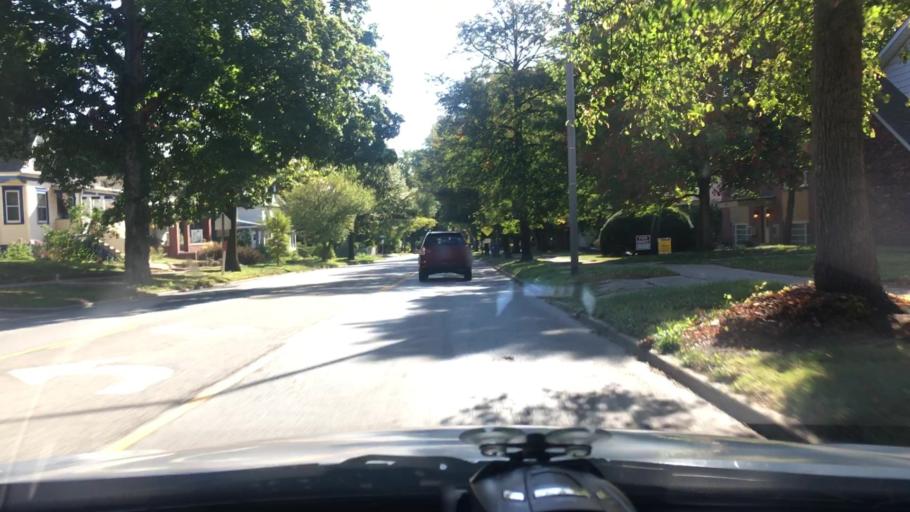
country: US
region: Illinois
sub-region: Champaign County
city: Champaign
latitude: 40.1126
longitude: -88.2532
